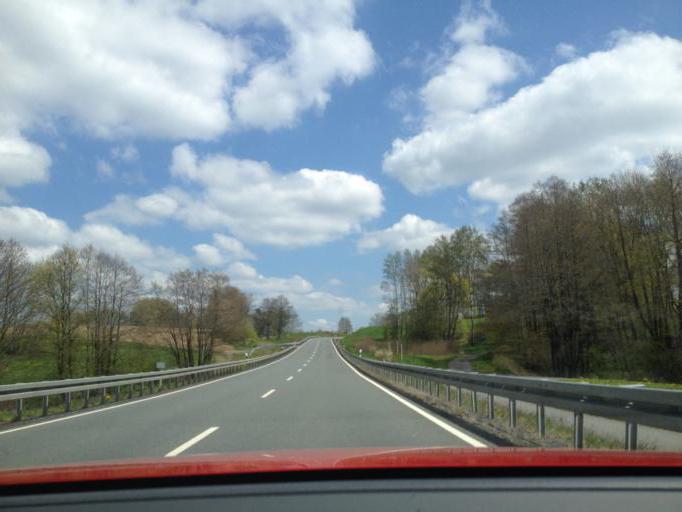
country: DE
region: Bavaria
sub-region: Upper Franconia
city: Marktredwitz
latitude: 49.9765
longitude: 12.0981
